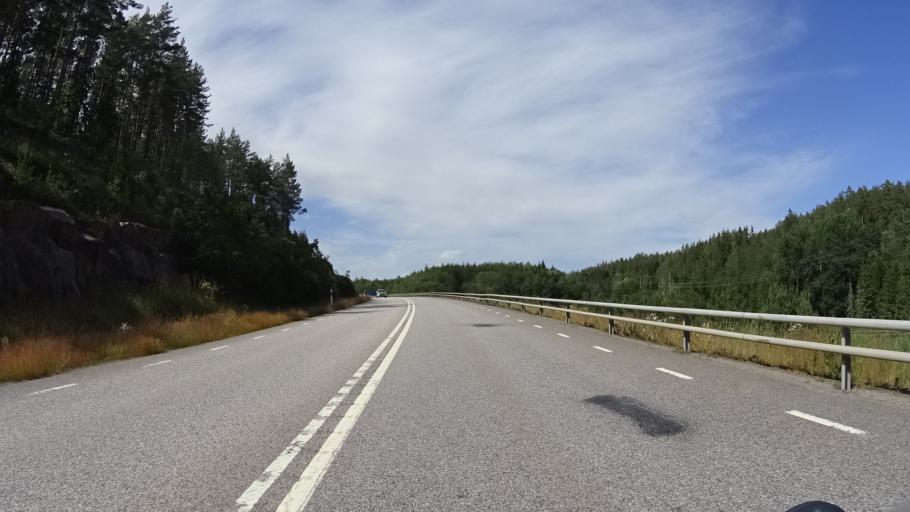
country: SE
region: Kalmar
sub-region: Vasterviks Kommun
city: Overum
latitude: 57.9714
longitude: 16.3369
